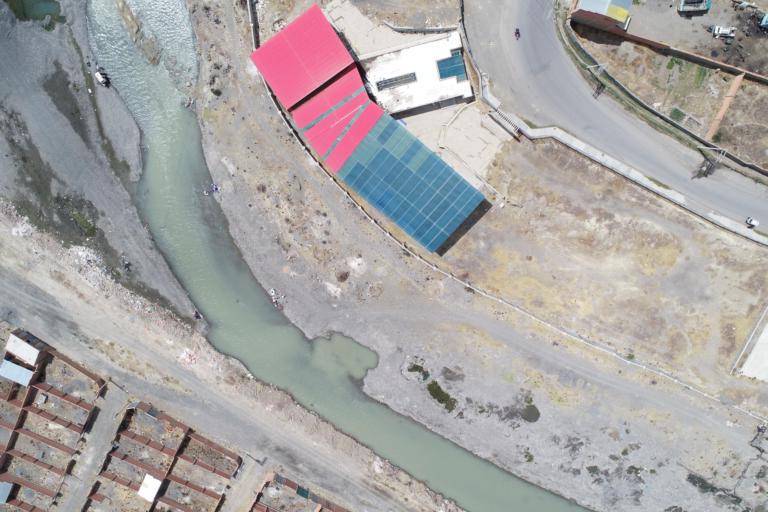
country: BO
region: La Paz
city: Achacachi
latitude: -16.0388
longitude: -68.6846
